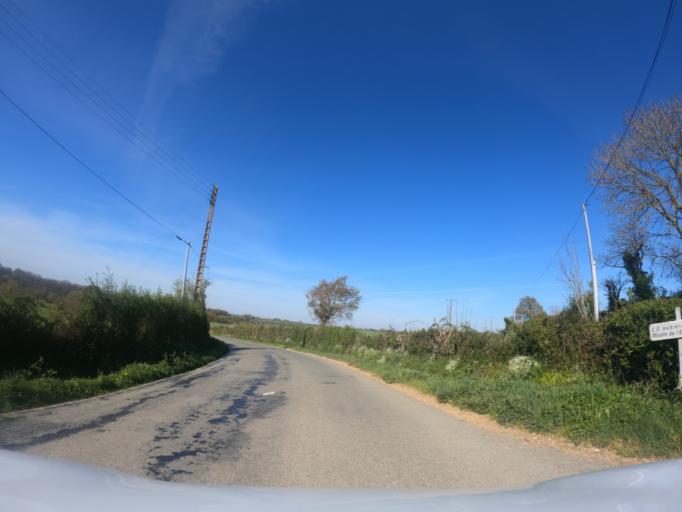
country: FR
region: Pays de la Loire
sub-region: Departement de la Vendee
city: Montournais
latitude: 46.7067
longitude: -0.7508
